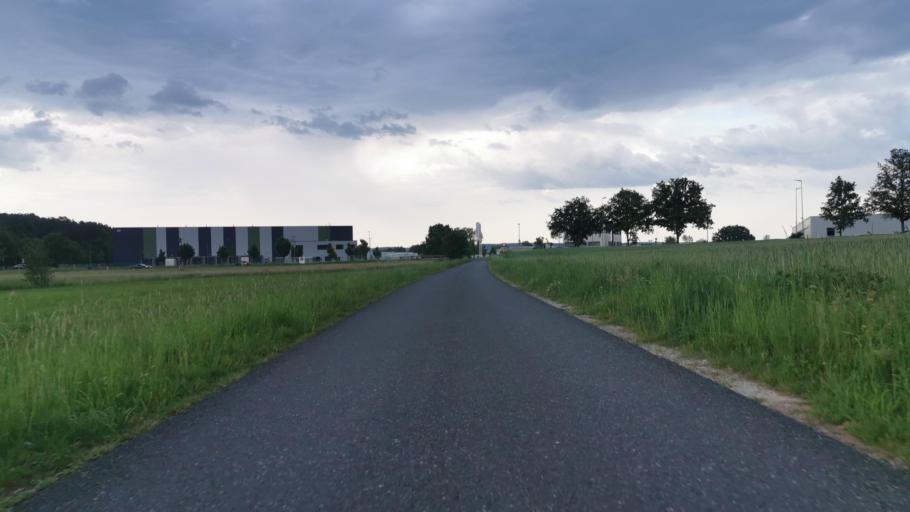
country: DE
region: Bavaria
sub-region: Regierungsbezirk Mittelfranken
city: Gremsdorf
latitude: 49.7105
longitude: 10.8359
